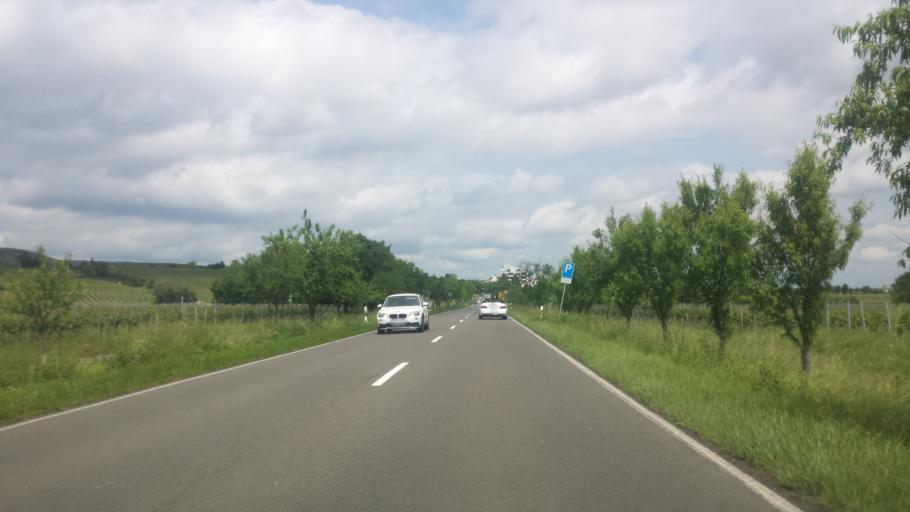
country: DE
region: Rheinland-Pfalz
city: Wachenheim
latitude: 49.4491
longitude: 8.1774
